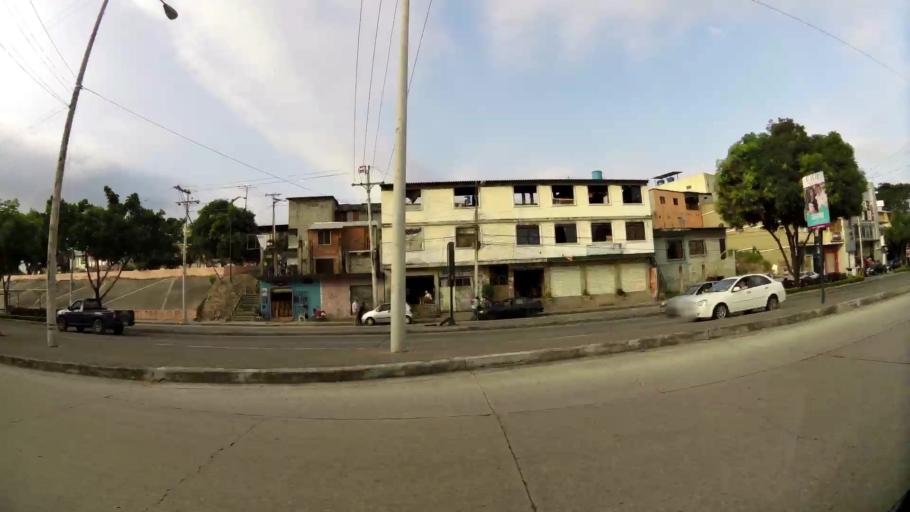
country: EC
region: Guayas
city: Eloy Alfaro
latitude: -2.1324
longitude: -79.8965
